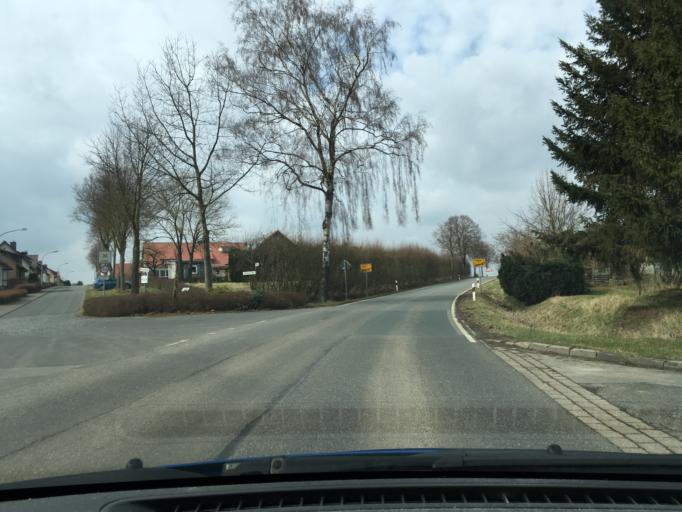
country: DE
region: Lower Saxony
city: Adelebsen
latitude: 51.5397
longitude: 9.7391
